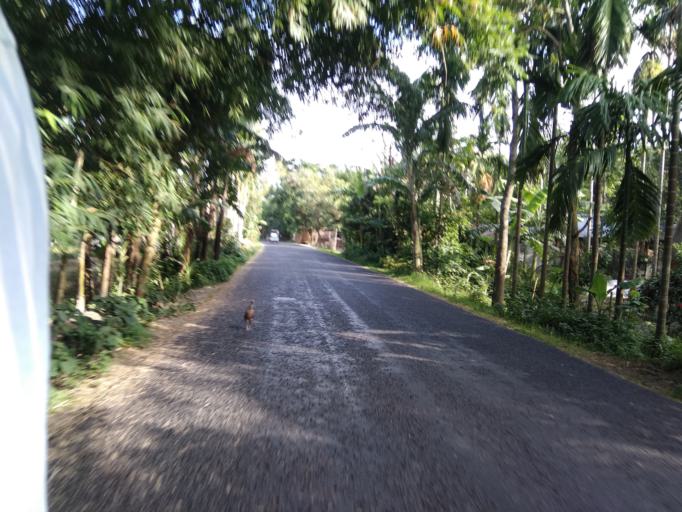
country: BD
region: Rangpur Division
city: Rangpur
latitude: 25.8380
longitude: 89.1142
